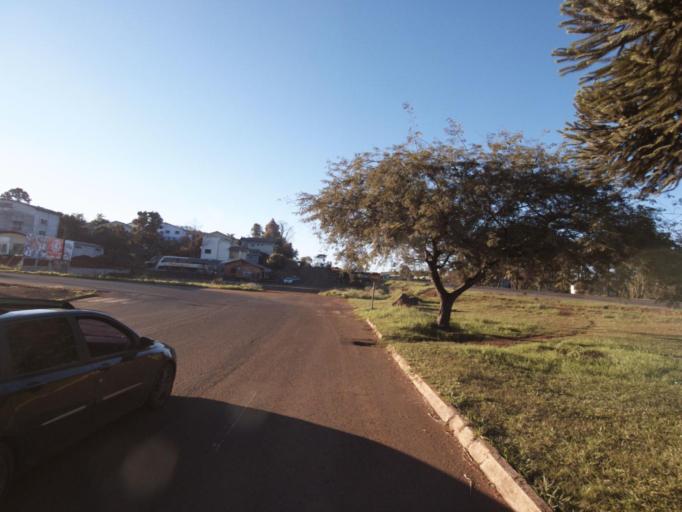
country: BR
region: Santa Catarina
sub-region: Chapeco
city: Chapeco
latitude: -26.8517
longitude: -52.9803
